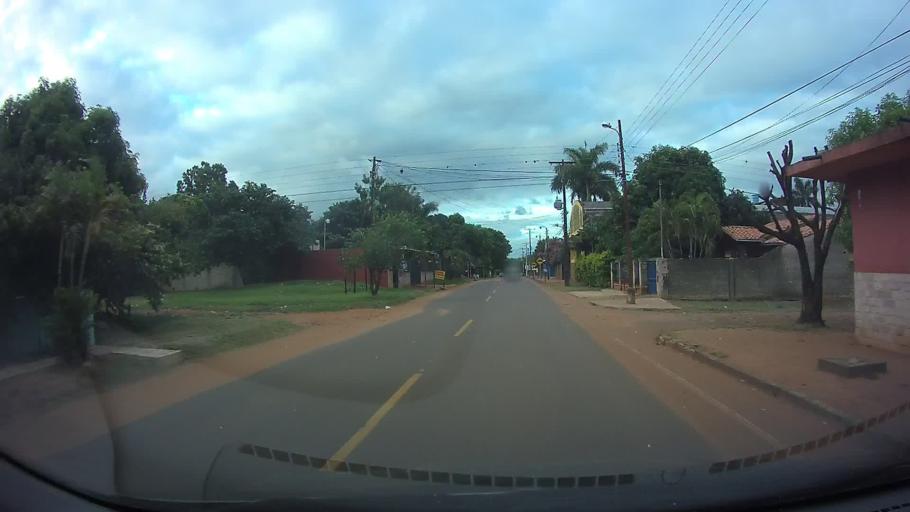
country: PY
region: Central
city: San Lorenzo
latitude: -25.2853
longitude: -57.4868
